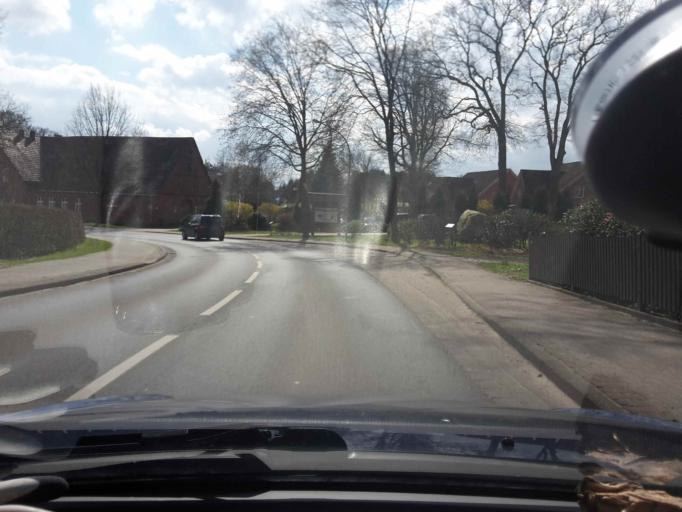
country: DE
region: Lower Saxony
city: Asendorf
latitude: 53.2912
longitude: 9.9767
